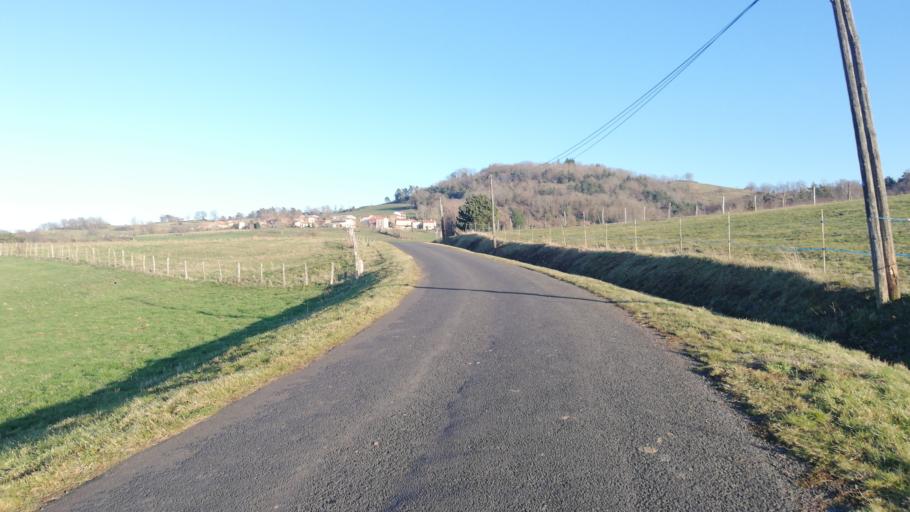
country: FR
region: Auvergne
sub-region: Departement du Puy-de-Dome
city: Billom
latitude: 45.6866
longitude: 3.3732
